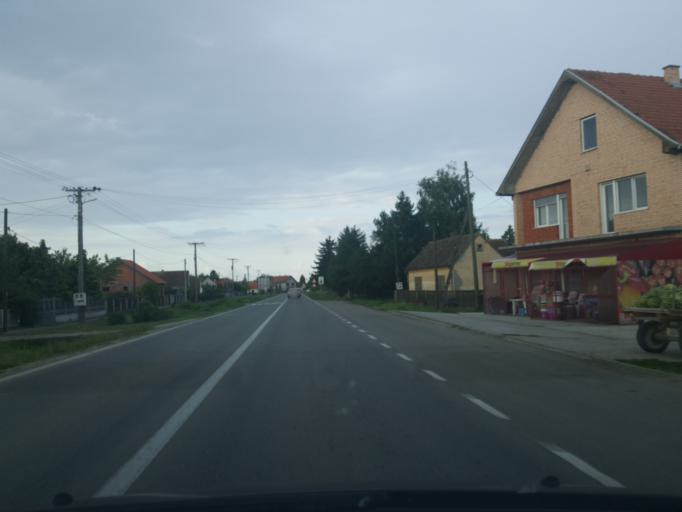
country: RS
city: Ribari
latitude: 44.7277
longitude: 19.4518
